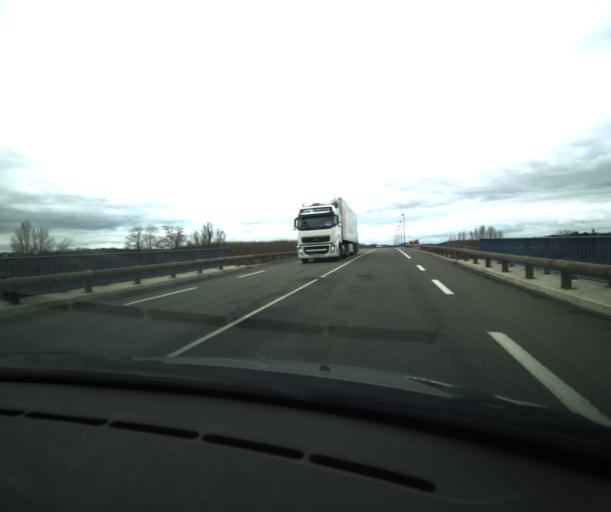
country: FR
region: Midi-Pyrenees
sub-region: Departement du Tarn-et-Garonne
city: Moissac
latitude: 44.0892
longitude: 1.1139
